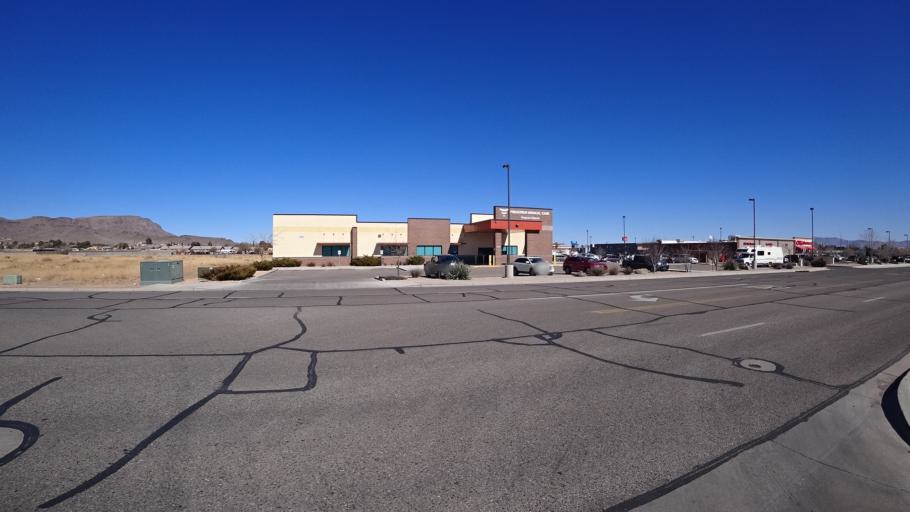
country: US
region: Arizona
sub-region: Mohave County
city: Kingman
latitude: 35.2248
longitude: -114.0382
